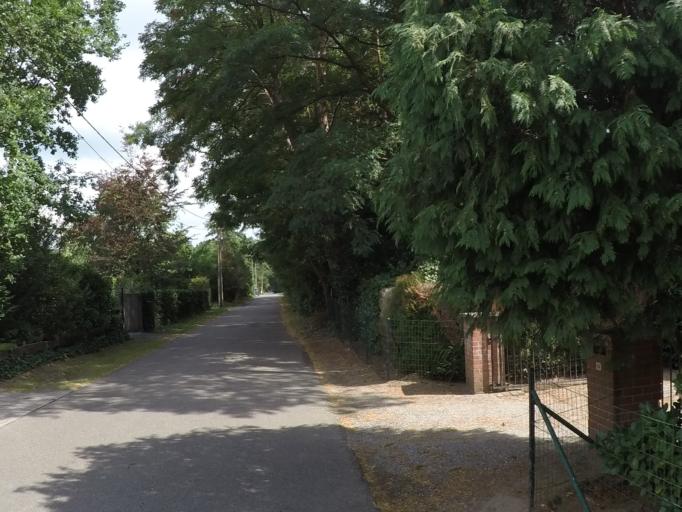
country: BE
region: Flanders
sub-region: Provincie Antwerpen
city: Zandhoven
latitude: 51.1951
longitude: 4.6821
